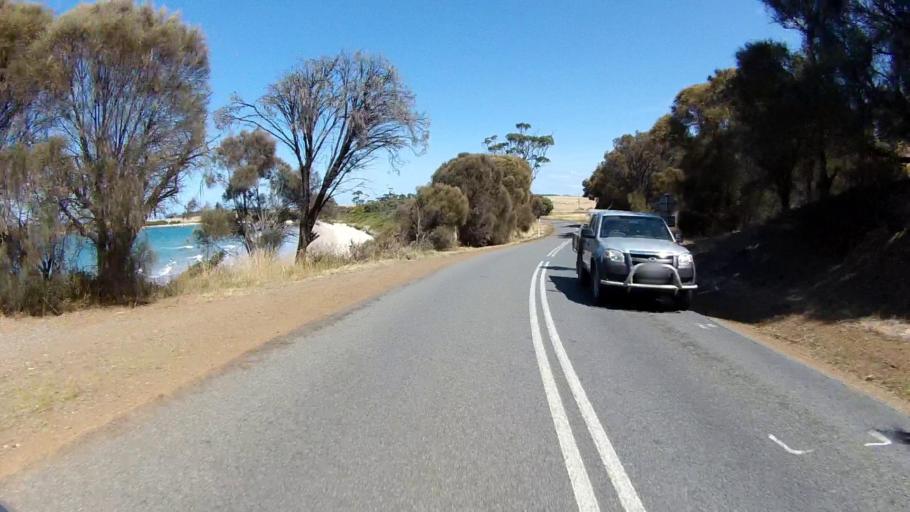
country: AU
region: Tasmania
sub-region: Sorell
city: Sorell
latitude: -42.2421
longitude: 148.0123
